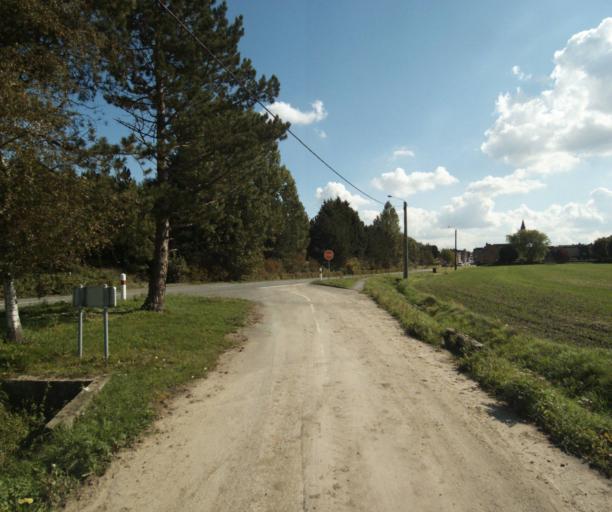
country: FR
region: Nord-Pas-de-Calais
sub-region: Departement du Nord
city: Illies
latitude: 50.5655
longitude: 2.8292
